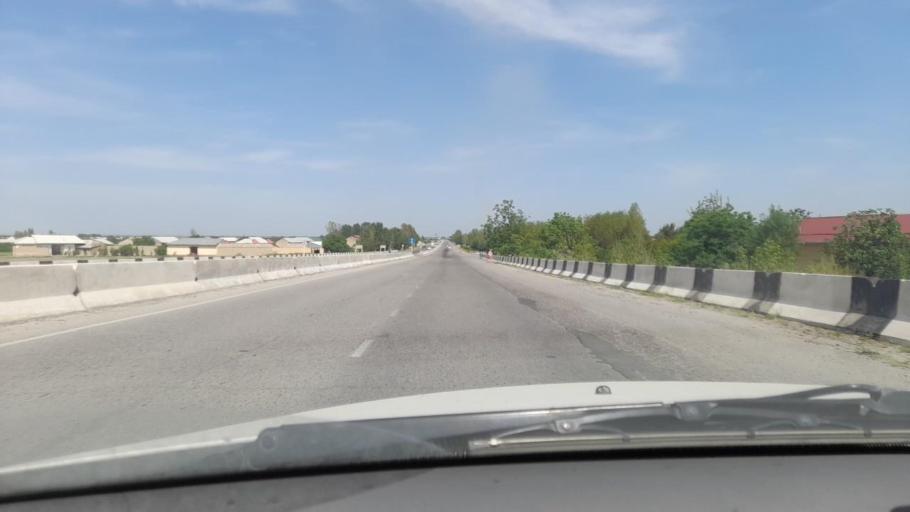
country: UZ
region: Samarqand
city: Kattaqo'rg'on
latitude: 39.9158
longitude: 66.3206
